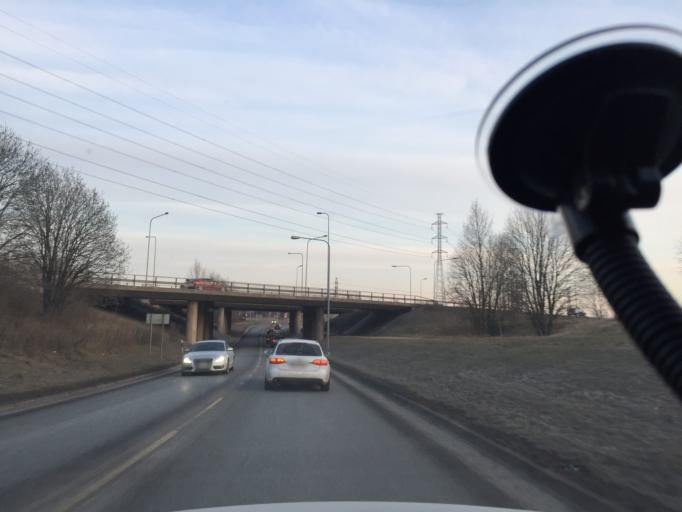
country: FI
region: Uusimaa
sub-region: Helsinki
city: Vantaa
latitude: 60.2689
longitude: 24.9703
